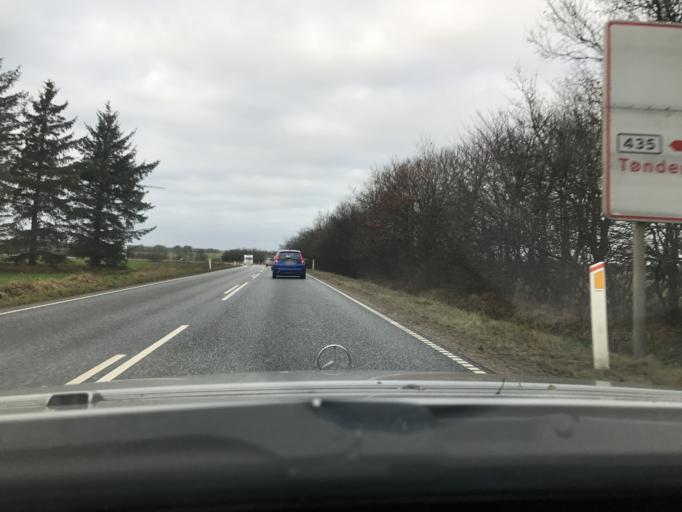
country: DK
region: South Denmark
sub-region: Tonder Kommune
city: Toftlund
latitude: 55.1073
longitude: 9.1811
